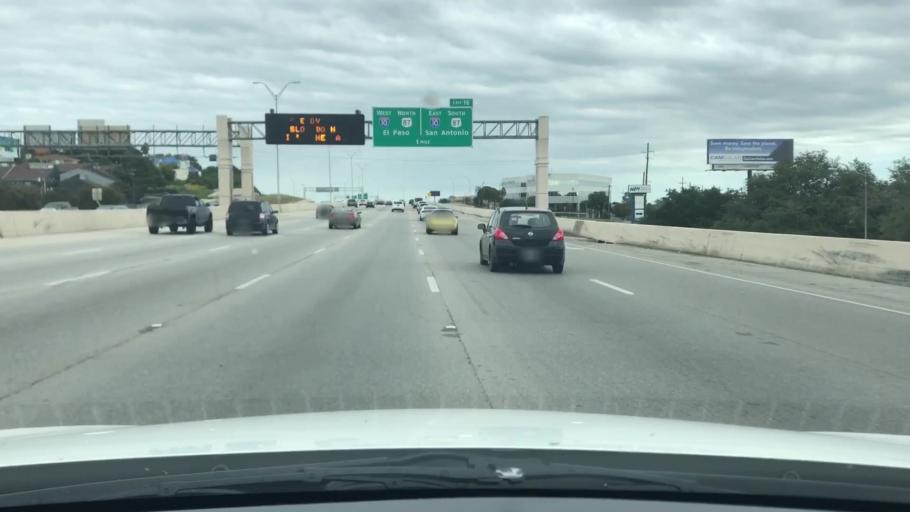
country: US
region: Texas
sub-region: Bexar County
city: Balcones Heights
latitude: 29.4893
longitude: -98.5692
